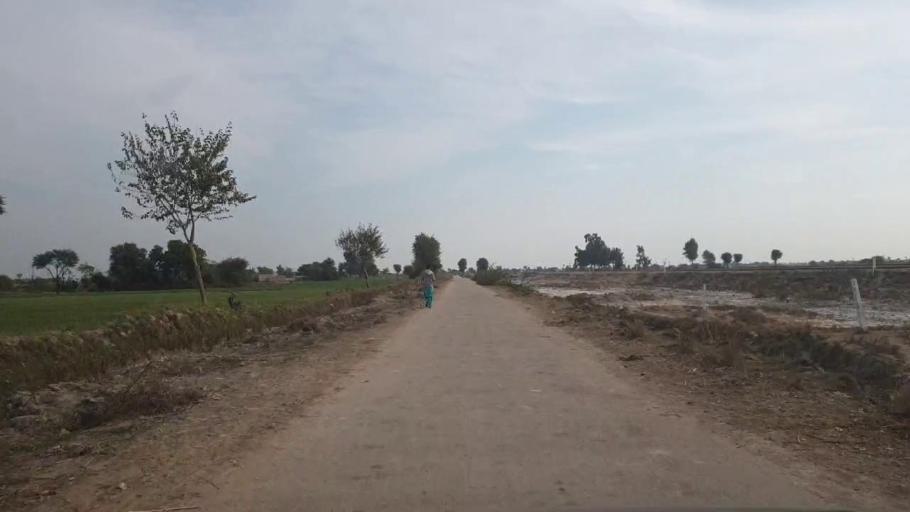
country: PK
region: Sindh
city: Nawabshah
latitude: 26.0896
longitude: 68.4847
